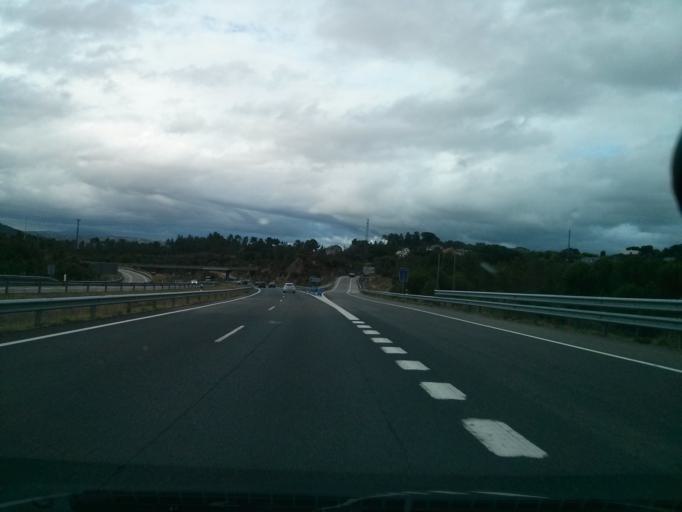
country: ES
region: Galicia
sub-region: Provincia de Ourense
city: Ourense
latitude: 42.3030
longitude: -7.8749
